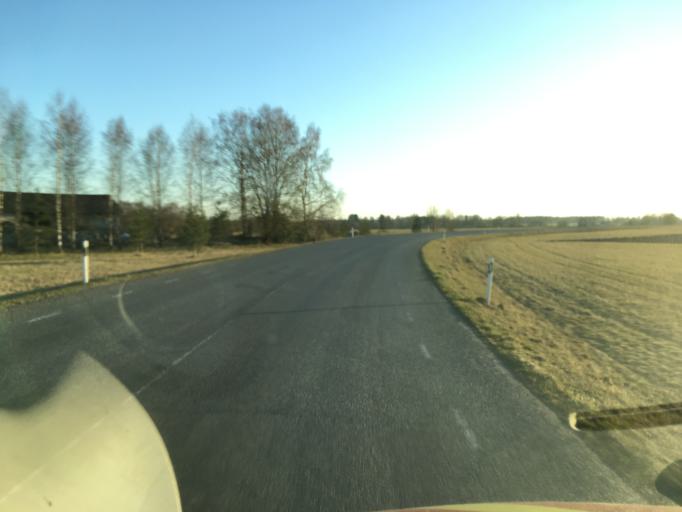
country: EE
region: Raplamaa
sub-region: Kehtna vald
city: Kehtna
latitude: 59.0103
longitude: 24.9189
